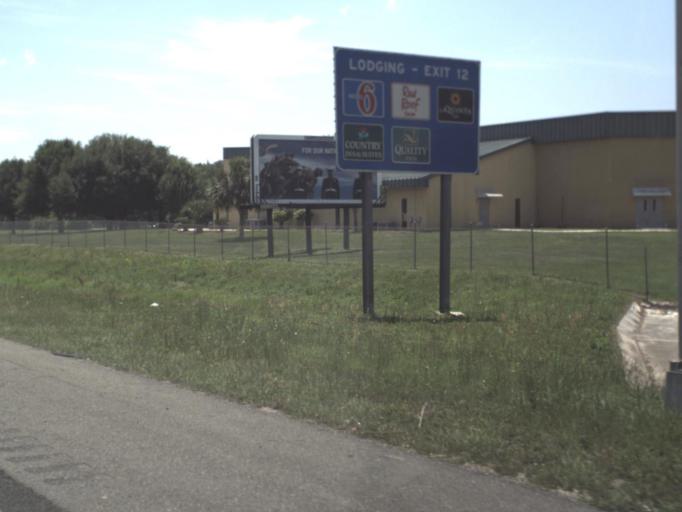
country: US
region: Florida
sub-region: Clay County
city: Bellair-Meadowbrook Terrace
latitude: 30.2308
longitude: -81.7631
